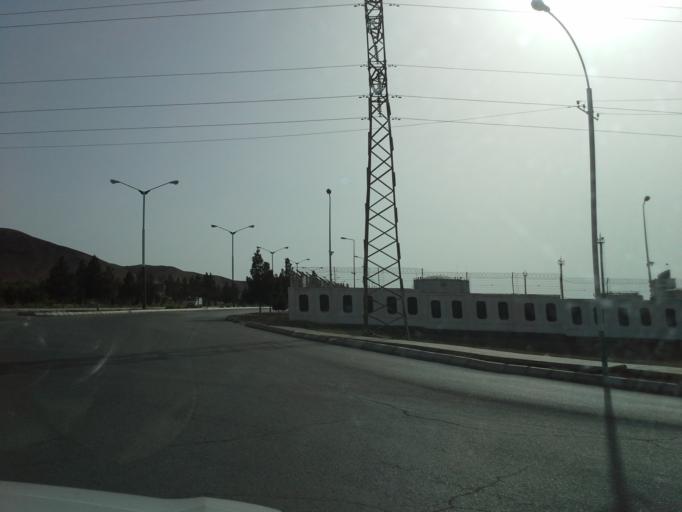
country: TM
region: Balkan
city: Turkmenbasy
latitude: 40.0195
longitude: 52.9703
